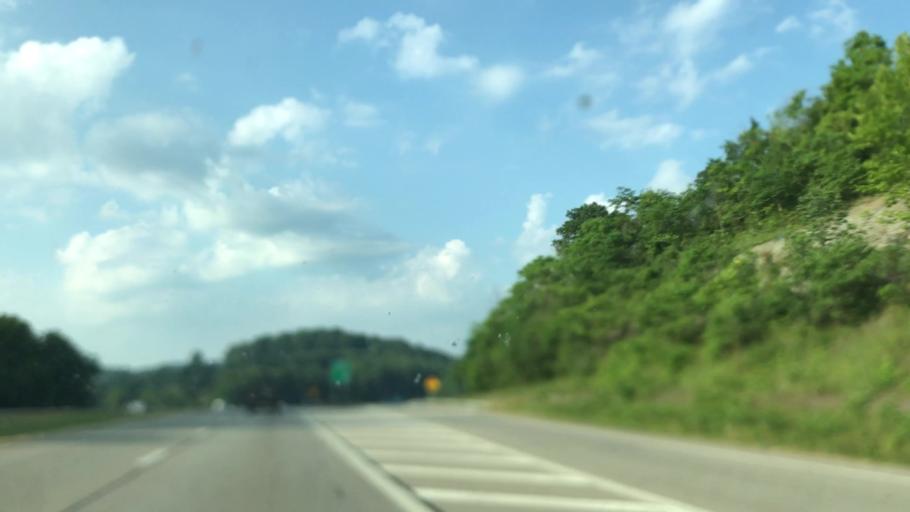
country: US
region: West Virginia
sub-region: Harrison County
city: Stonewood
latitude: 39.2310
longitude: -80.2974
